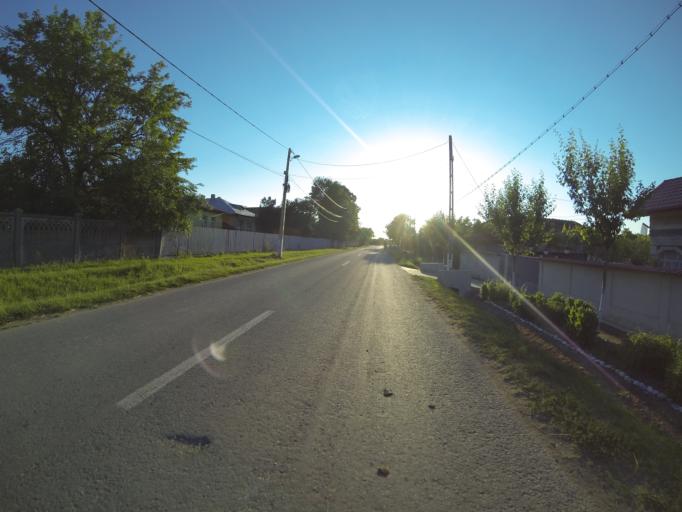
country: RO
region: Dolj
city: Satu Nou Calopar
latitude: 44.1624
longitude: 23.7653
